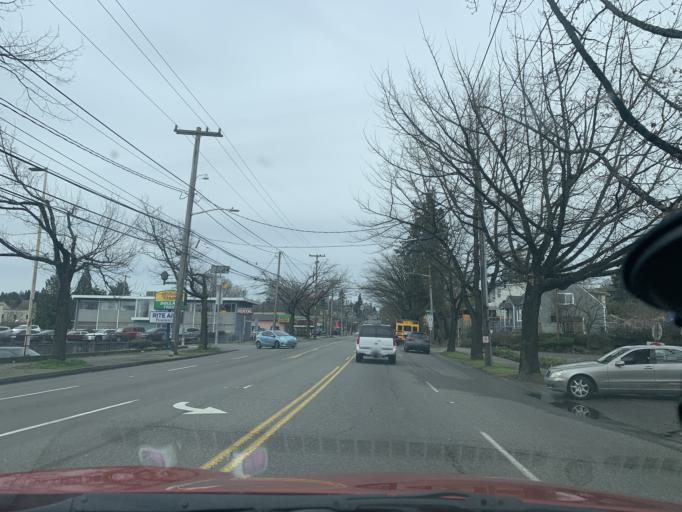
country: US
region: Washington
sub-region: King County
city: Bryn Mawr-Skyway
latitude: 47.5229
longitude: -122.2701
